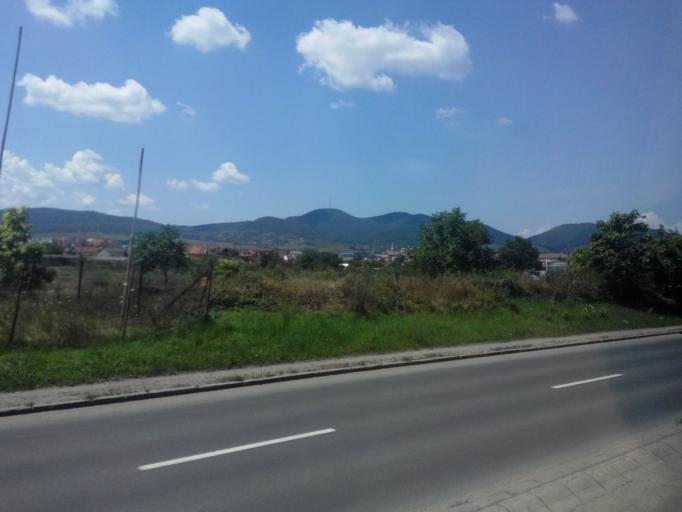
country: RO
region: Hunedoara
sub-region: Municipiul Deva
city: Deva
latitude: 45.8655
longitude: 22.9237
